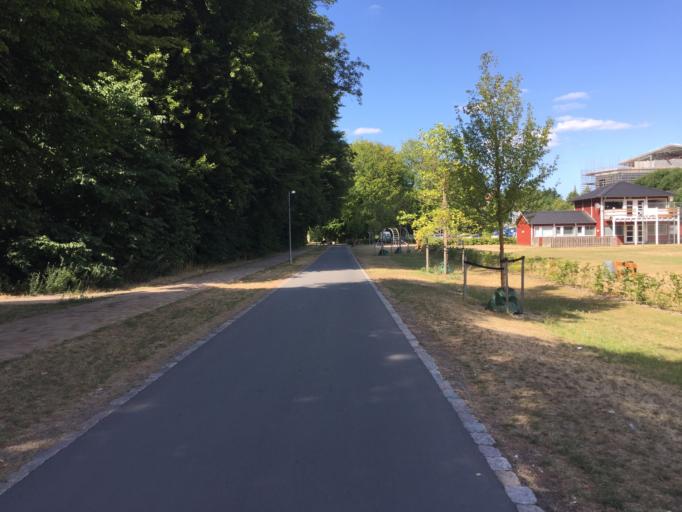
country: DK
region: South Denmark
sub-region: Odense Kommune
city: Odense
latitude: 55.3904
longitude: 10.3843
